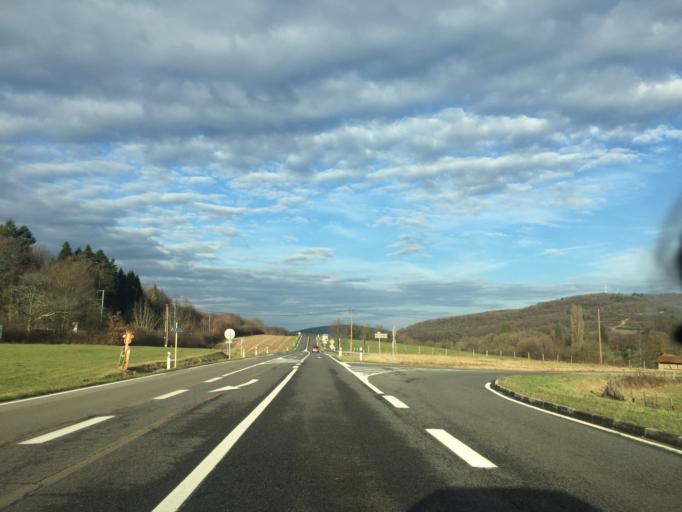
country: FR
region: Franche-Comte
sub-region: Departement du Jura
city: Mouchard
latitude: 46.9449
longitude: 5.7807
